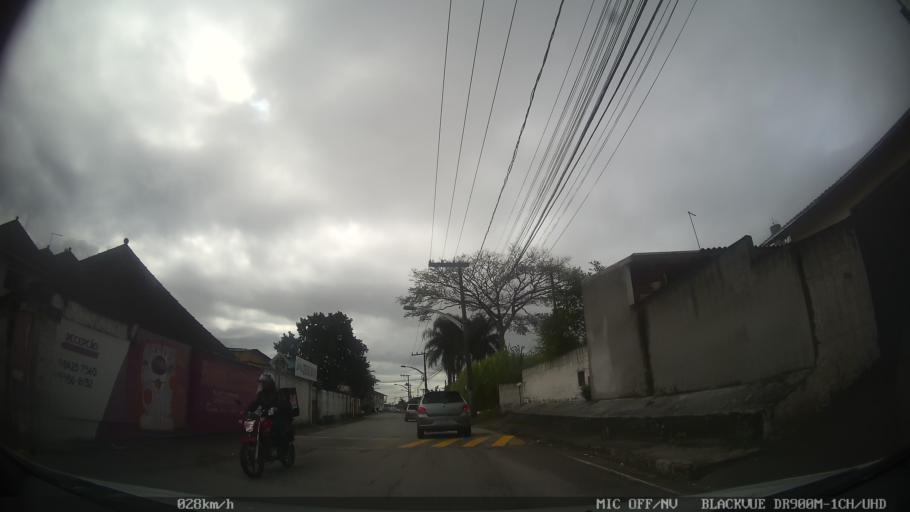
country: BR
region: Santa Catarina
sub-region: Biguacu
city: Biguacu
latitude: -27.5334
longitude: -48.6392
